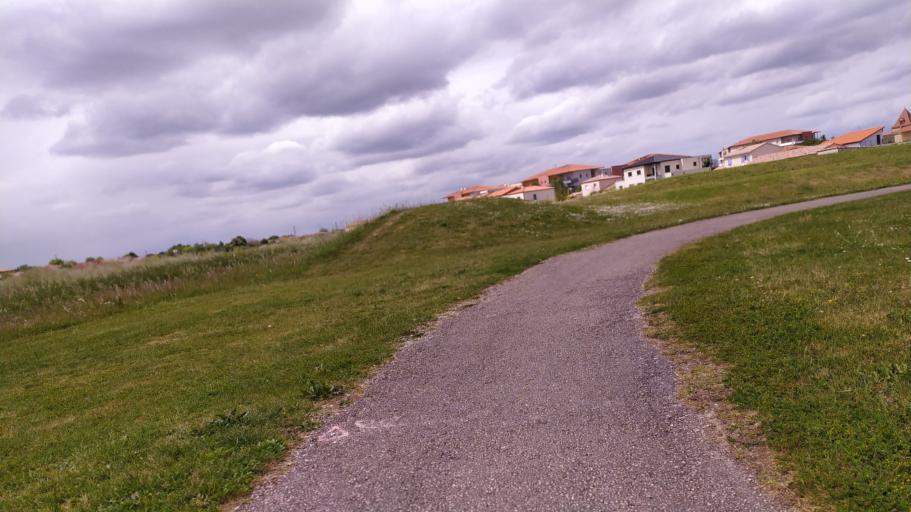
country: FR
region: Midi-Pyrenees
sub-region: Departement de la Haute-Garonne
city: Plaisance-du-Touch
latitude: 43.5811
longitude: 1.2897
